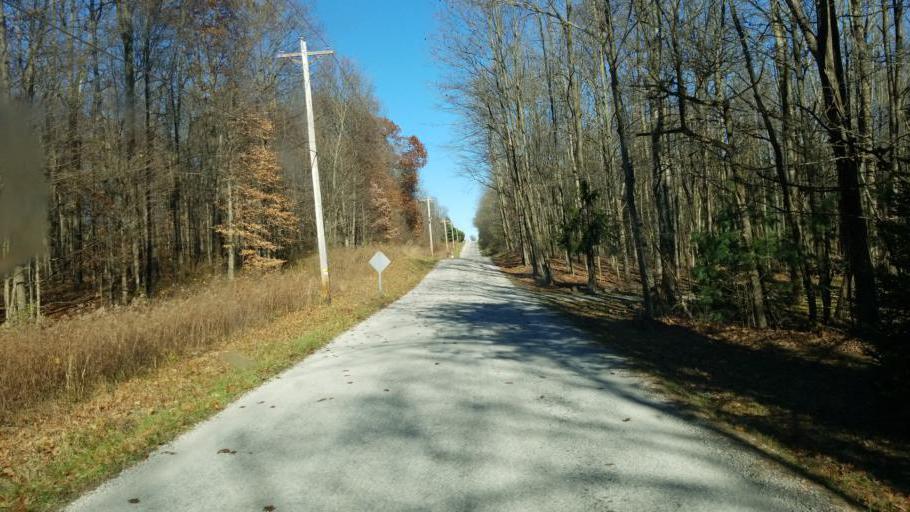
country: US
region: Ohio
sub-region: Ashland County
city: Ashland
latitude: 40.8551
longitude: -82.3877
